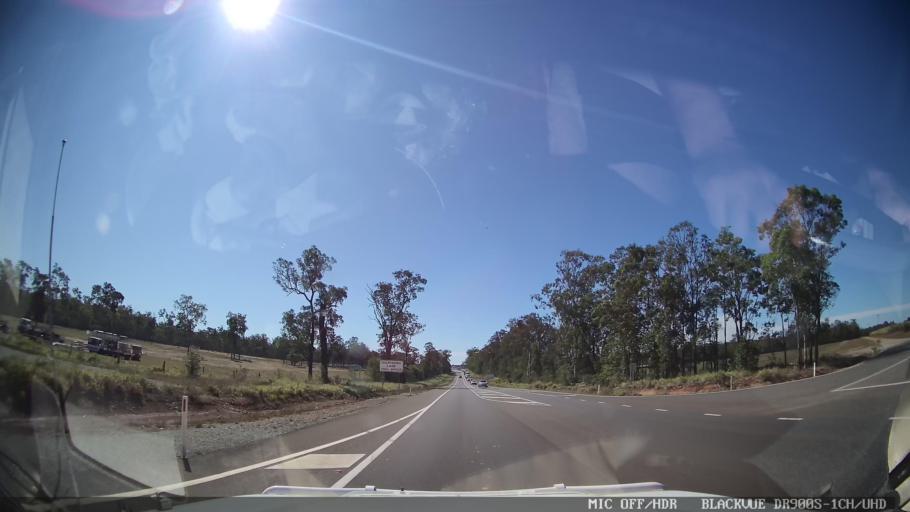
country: AU
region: Queensland
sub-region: Fraser Coast
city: Maryborough
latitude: -25.6513
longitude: 152.6325
